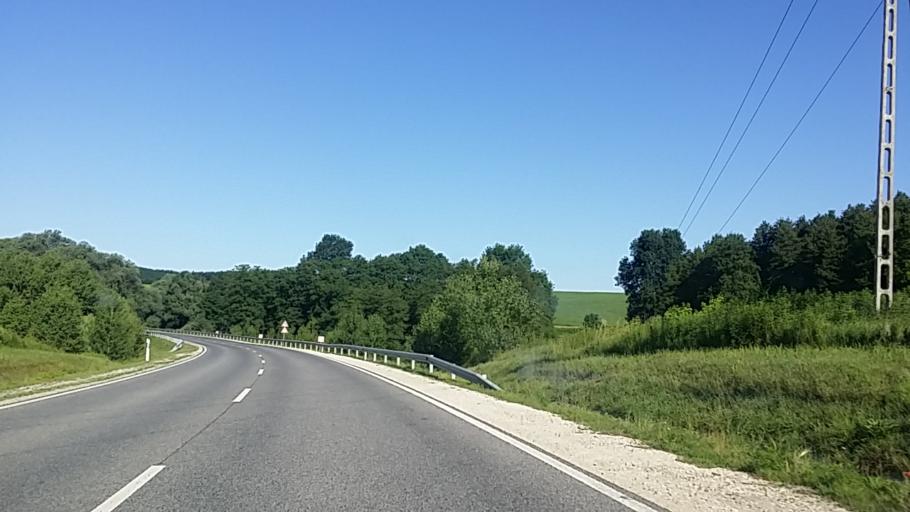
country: HU
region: Zala
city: Zalaszentgrot
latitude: 46.8360
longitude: 17.0351
